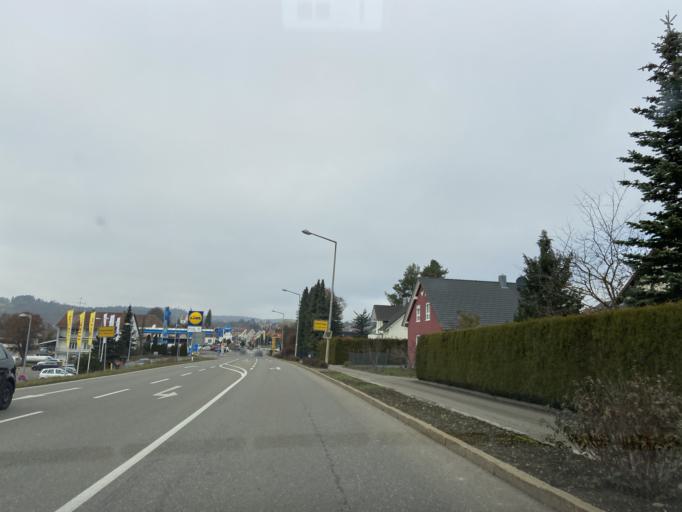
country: DE
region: Baden-Wuerttemberg
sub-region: Tuebingen Region
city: Gammertingen
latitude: 48.2449
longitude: 9.2245
